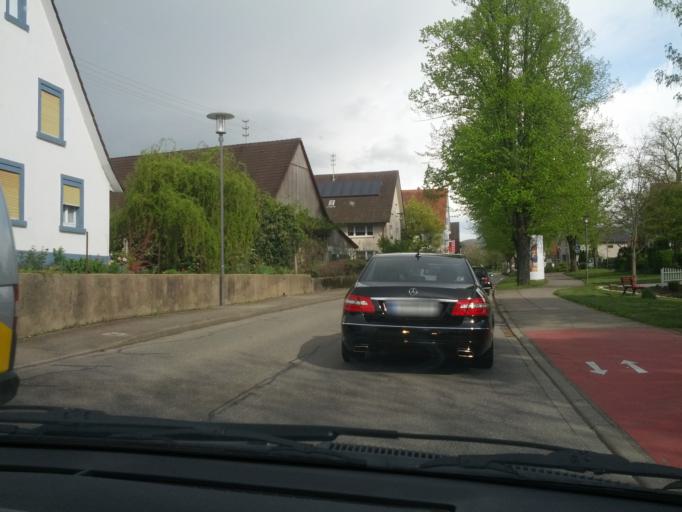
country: DE
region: Baden-Wuerttemberg
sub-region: Freiburg Region
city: Denzlingen
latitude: 48.0664
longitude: 7.8856
